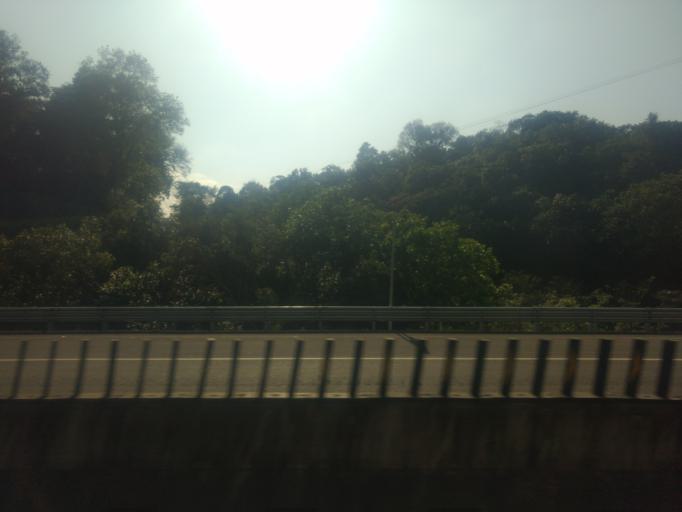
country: MX
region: Puebla
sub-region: Xicotepec
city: San Lorenzo
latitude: 20.3875
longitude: -97.9461
